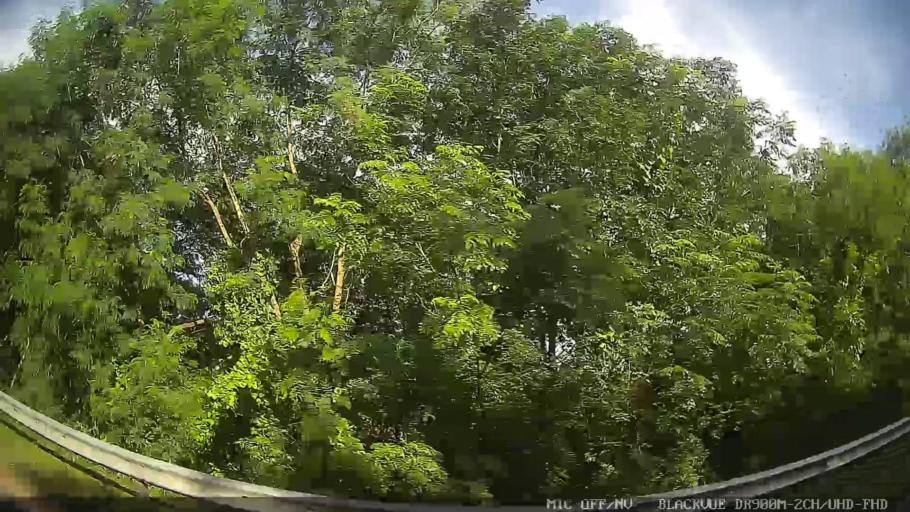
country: BR
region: Sao Paulo
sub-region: Tiete
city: Tiete
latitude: -23.1109
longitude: -47.6963
